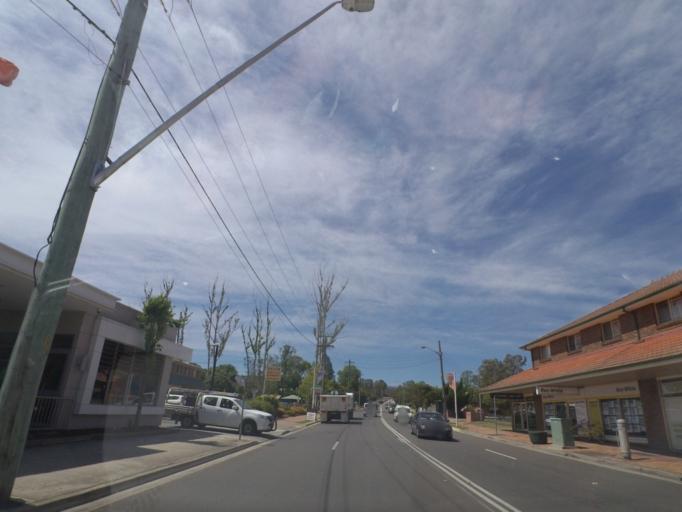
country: AU
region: New South Wales
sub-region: Wollondilly
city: Picton
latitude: -34.1674
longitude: 150.6124
